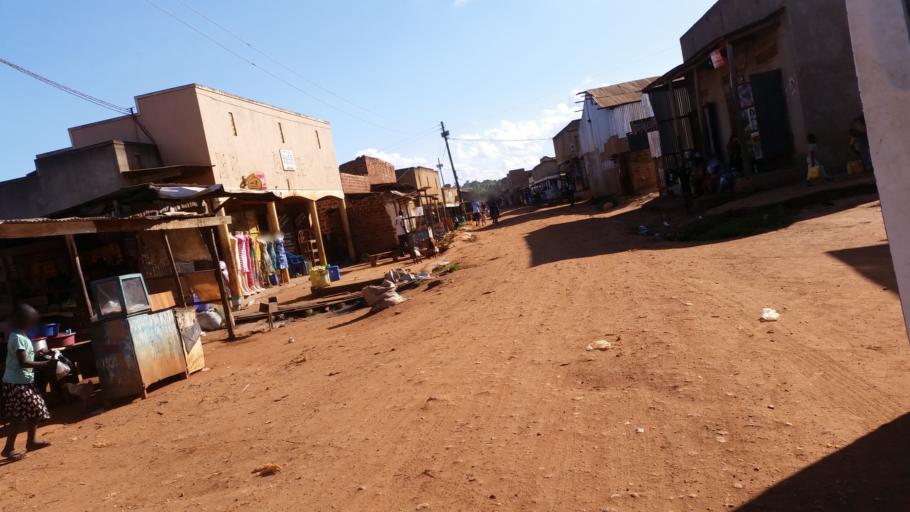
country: UG
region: Central Region
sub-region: Wakiso District
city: Kireka
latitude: 0.3288
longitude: 32.6495
